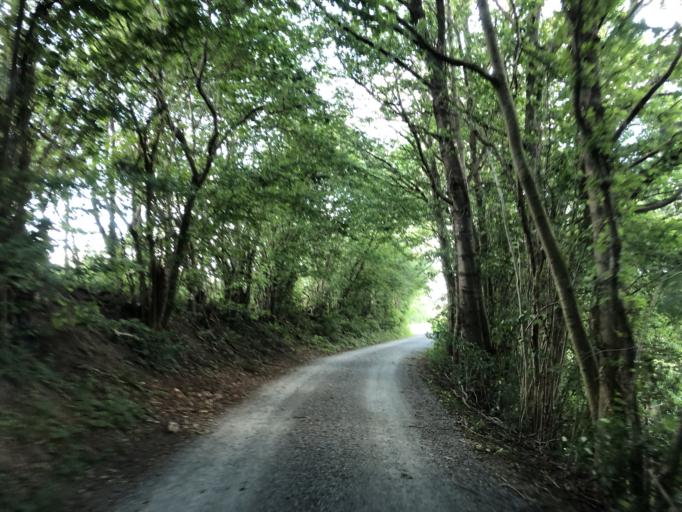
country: DK
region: South Denmark
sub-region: Vejle Kommune
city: Brejning
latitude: 55.6749
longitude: 9.6573
